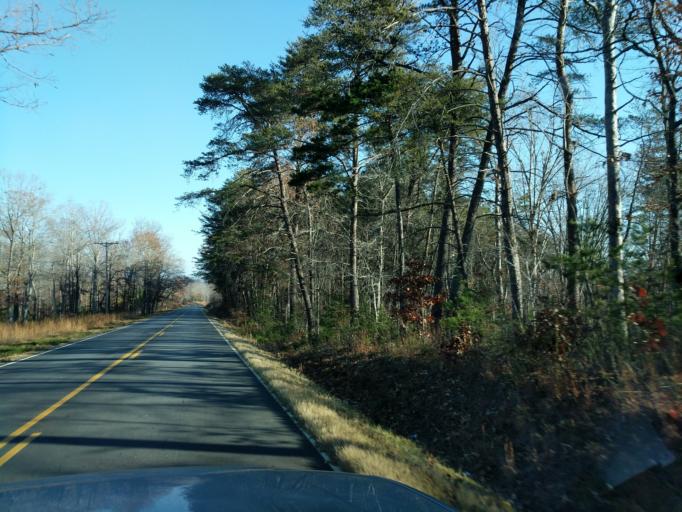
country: US
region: North Carolina
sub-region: Polk County
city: Columbus
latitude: 35.2637
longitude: -82.0607
